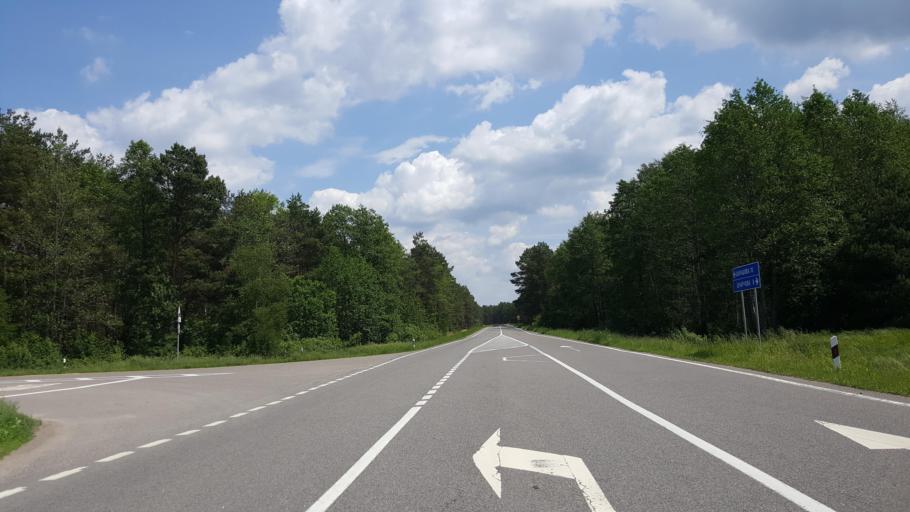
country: BY
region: Brest
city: Zhabinka
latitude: 52.4657
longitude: 24.1471
